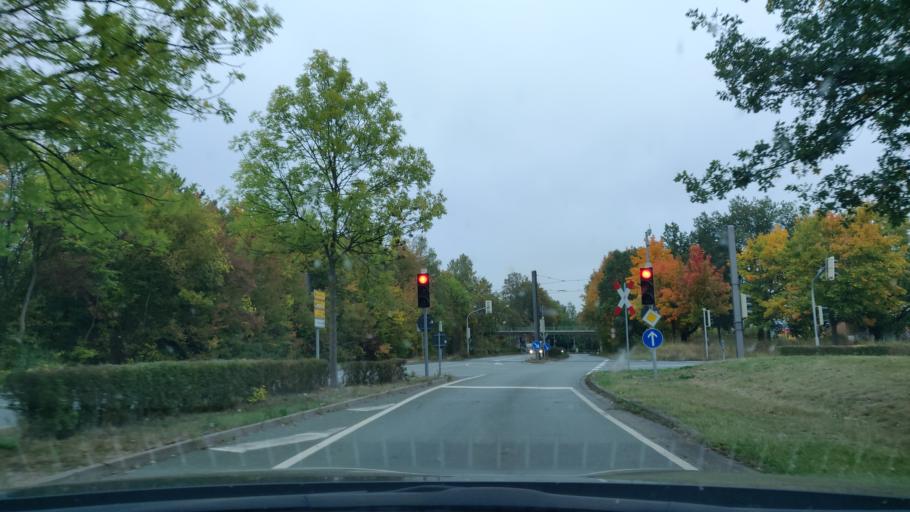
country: DE
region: Hesse
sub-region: Regierungsbezirk Kassel
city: Baunatal
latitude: 51.2628
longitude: 9.4238
